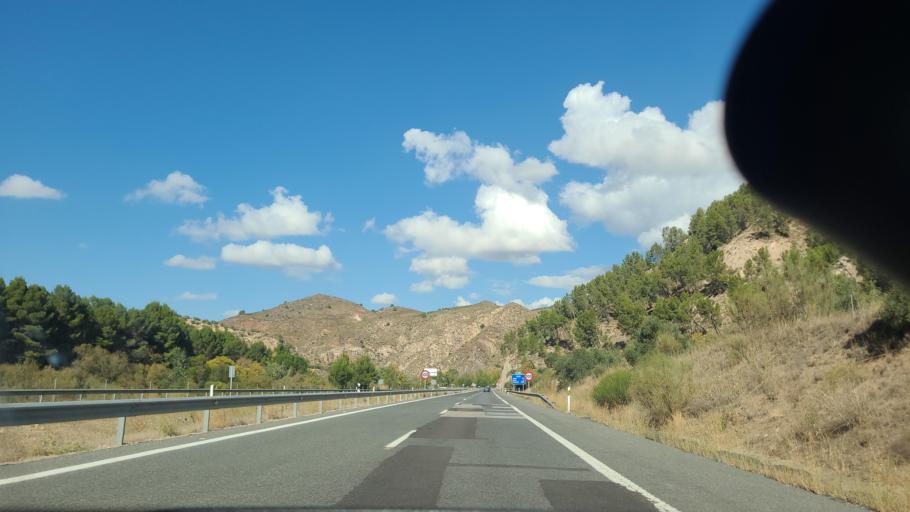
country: ES
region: Andalusia
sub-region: Provincia de Jaen
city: Cambil
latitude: 37.6497
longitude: -3.6062
